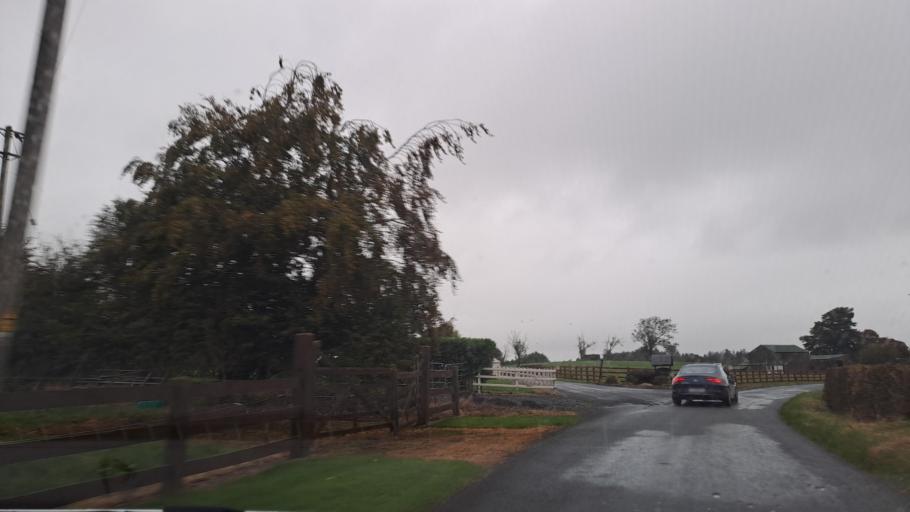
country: IE
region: Ulster
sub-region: County Monaghan
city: Monaghan
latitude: 54.2110
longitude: -6.9092
